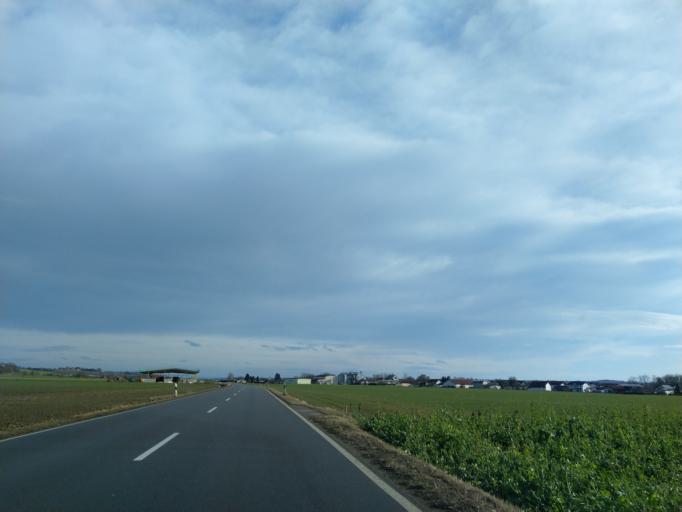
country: DE
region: Bavaria
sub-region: Lower Bavaria
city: Aldersbach
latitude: 48.6119
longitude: 13.0336
